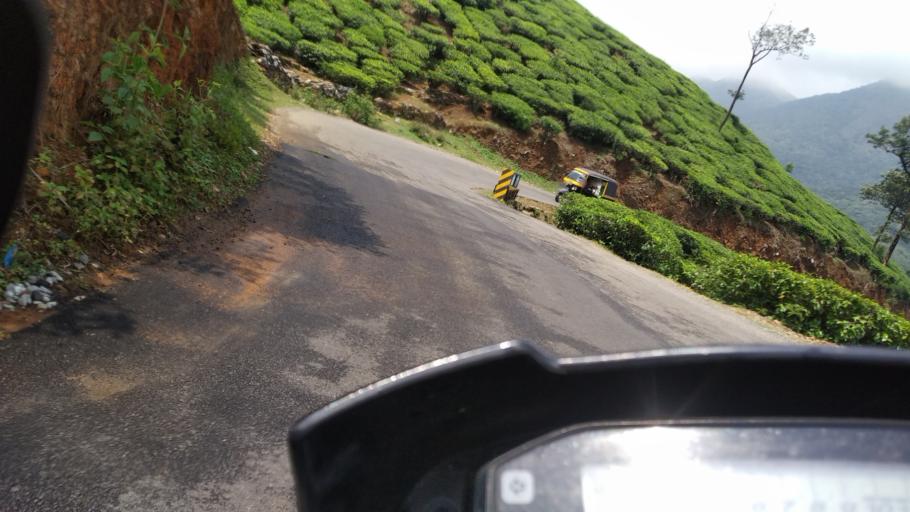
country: IN
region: Kerala
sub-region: Kottayam
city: Erattupetta
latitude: 9.6260
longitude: 76.9692
